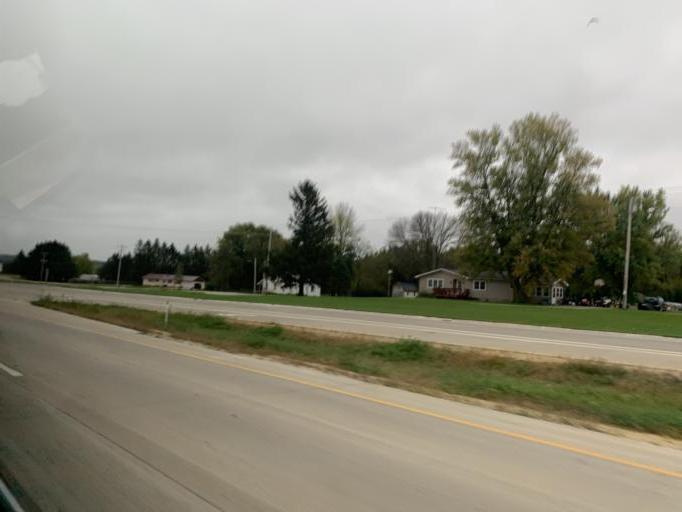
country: US
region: Wisconsin
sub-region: Crawford County
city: Prairie du Chien
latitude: 43.0119
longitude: -91.0713
